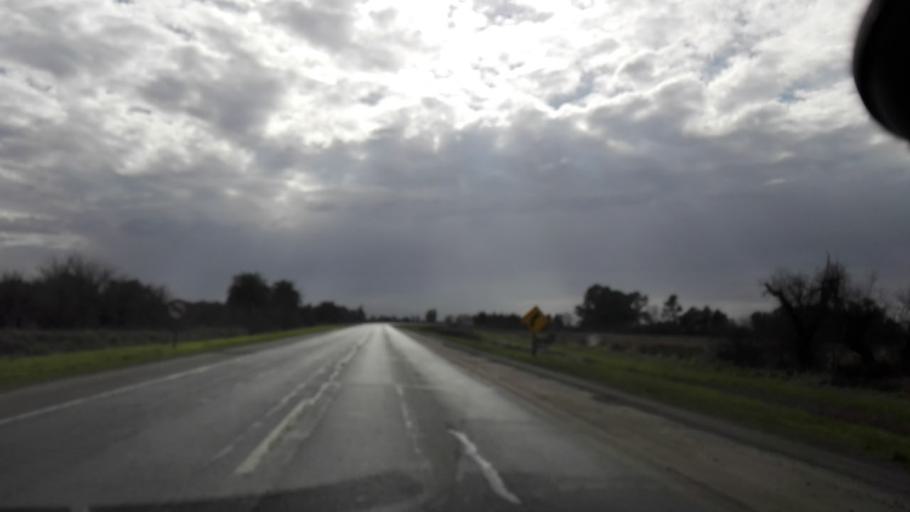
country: AR
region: Buenos Aires
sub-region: Partido de Las Flores
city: Las Flores
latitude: -36.0037
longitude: -59.0651
